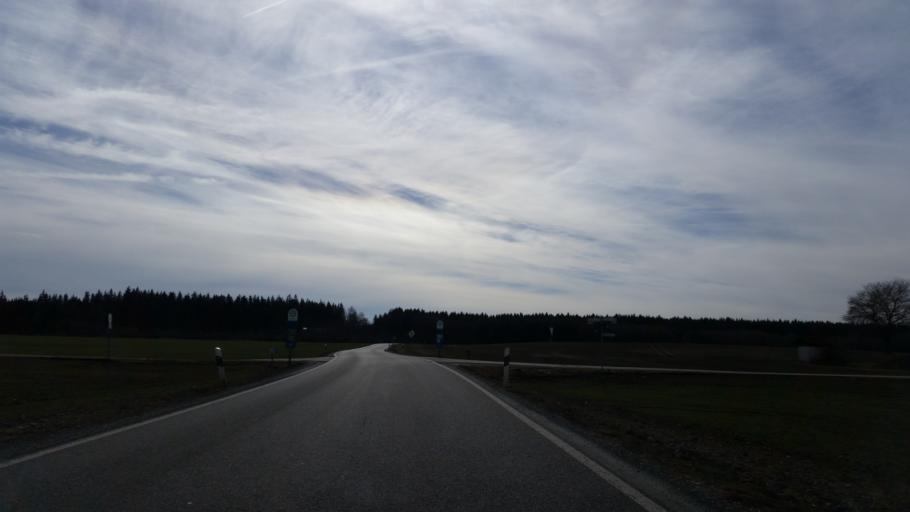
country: DE
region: Bavaria
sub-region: Upper Bavaria
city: Oberpframmern
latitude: 48.0483
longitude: 11.8163
